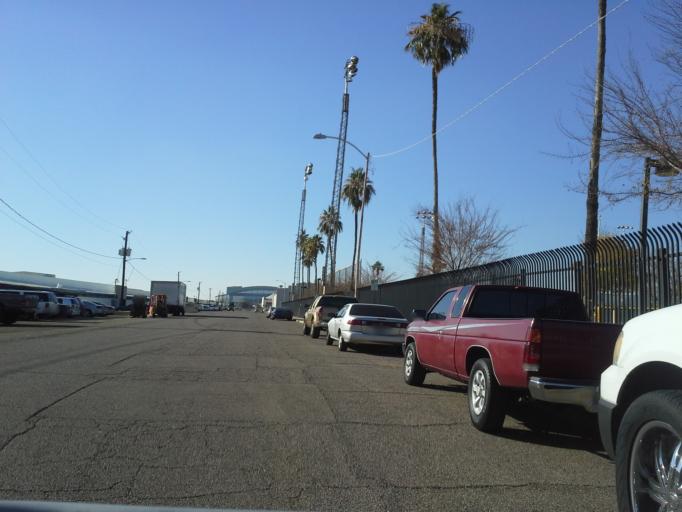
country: US
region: Arizona
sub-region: Maricopa County
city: Phoenix
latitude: 33.4452
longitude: -112.0483
